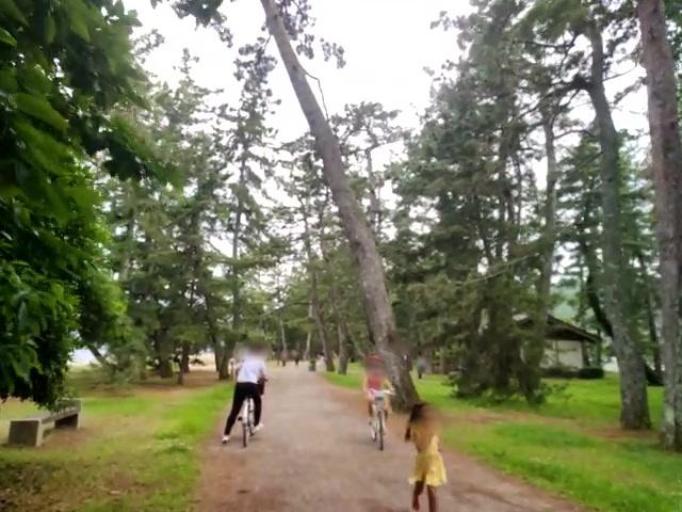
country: JP
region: Kyoto
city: Miyazu
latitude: 35.5620
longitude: 135.1878
